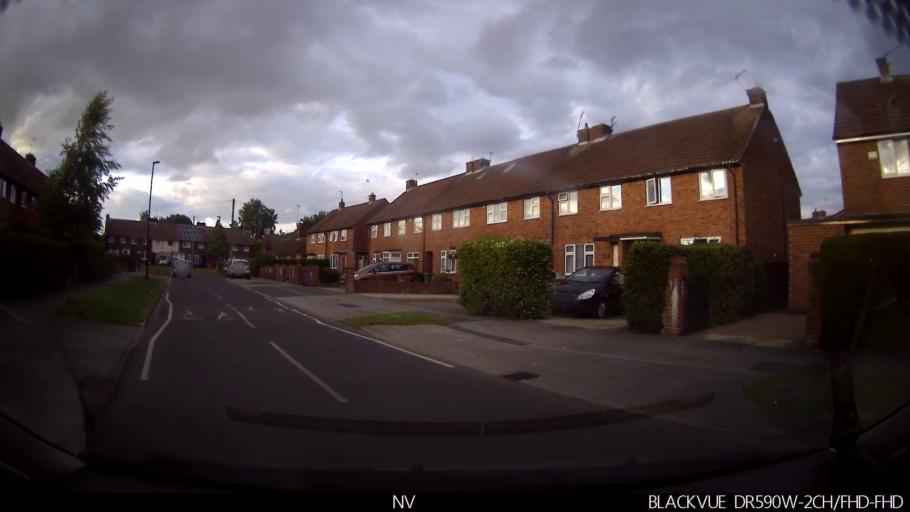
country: GB
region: England
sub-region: City of York
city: Nether Poppleton
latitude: 53.9544
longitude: -1.1394
